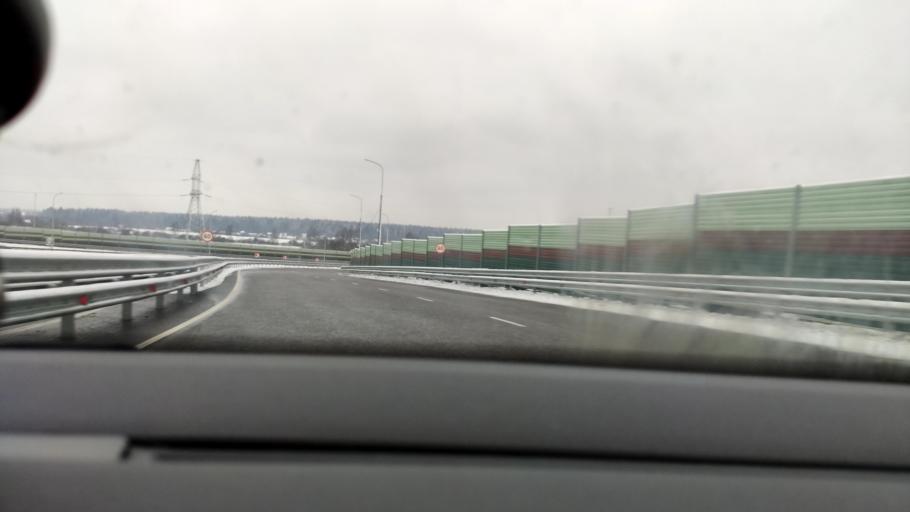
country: RU
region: Moskovskaya
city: Solnechnogorsk
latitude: 56.1656
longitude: 36.9292
